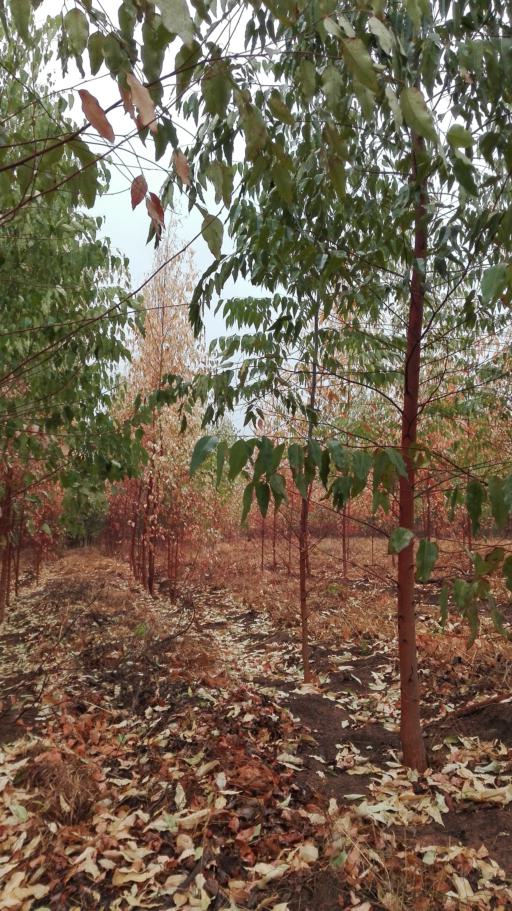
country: MZ
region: Nampula
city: Mutuali
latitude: -15.4670
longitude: 36.9782
